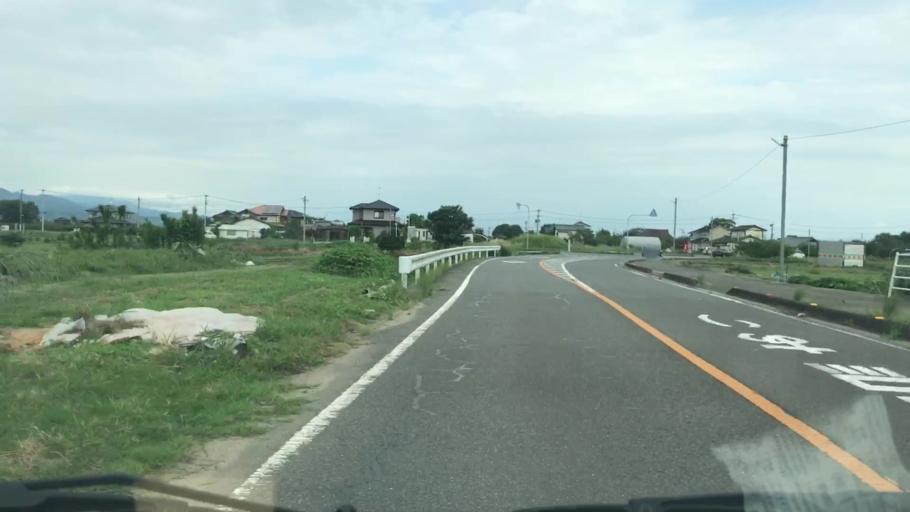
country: JP
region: Saga Prefecture
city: Saga-shi
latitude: 33.2884
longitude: 130.2479
